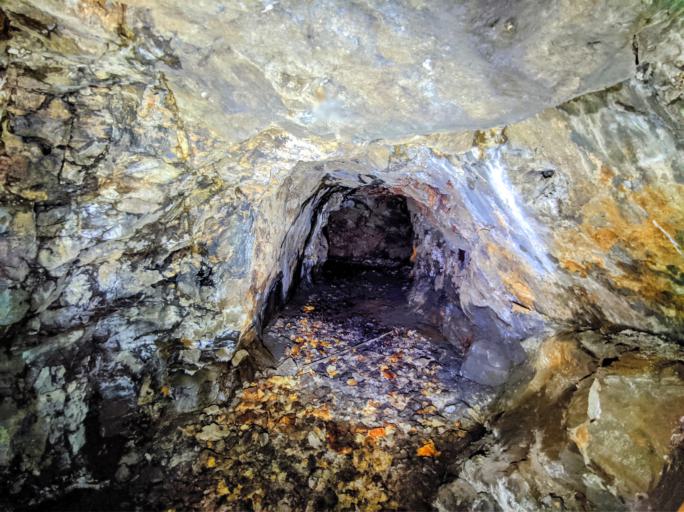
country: NO
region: Akershus
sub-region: Nittedal
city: Aneby
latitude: 60.1829
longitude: 10.8584
